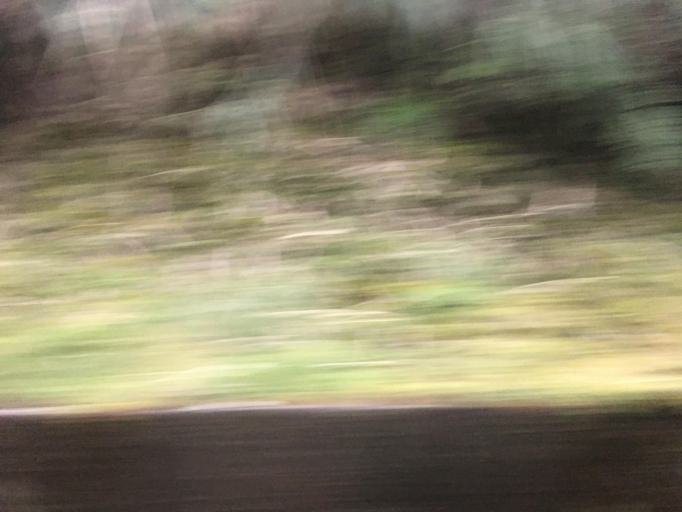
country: TW
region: Taiwan
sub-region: Yilan
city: Yilan
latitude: 24.5123
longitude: 121.5923
